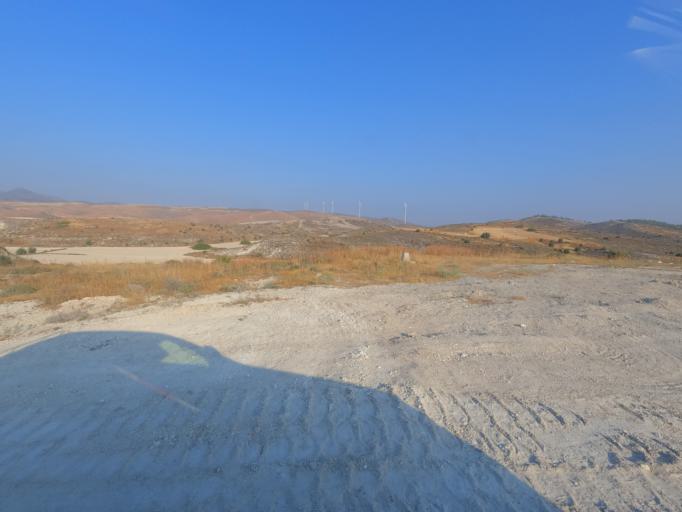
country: CY
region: Larnaka
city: Psevdas
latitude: 34.9223
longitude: 33.5145
